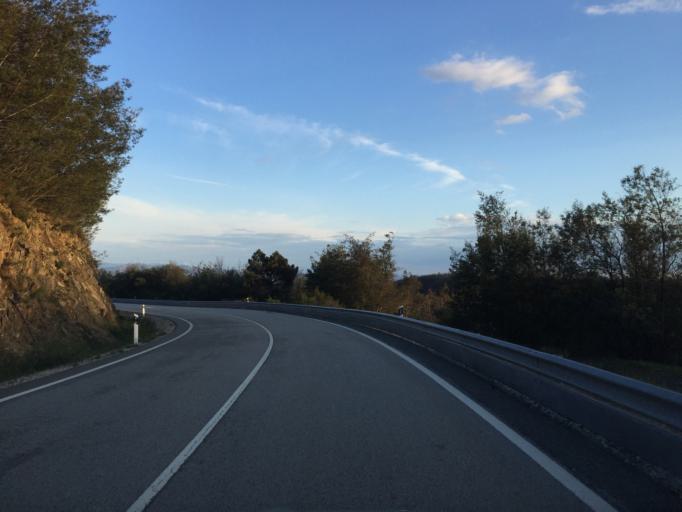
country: PT
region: Coimbra
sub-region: Pampilhosa da Serra
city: Pampilhosa da Serra
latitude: 40.1073
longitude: -8.0082
